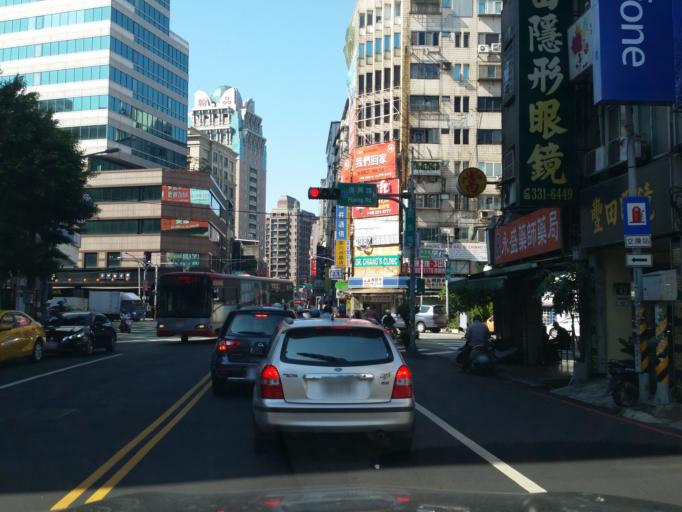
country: TW
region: Taiwan
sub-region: Taoyuan
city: Taoyuan
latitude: 24.9906
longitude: 121.3154
